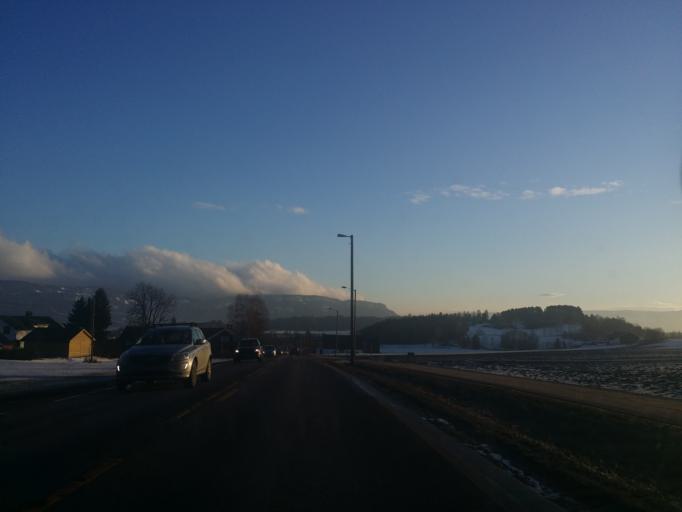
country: NO
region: Buskerud
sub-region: Hole
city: Vik
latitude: 60.1239
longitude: 10.2799
